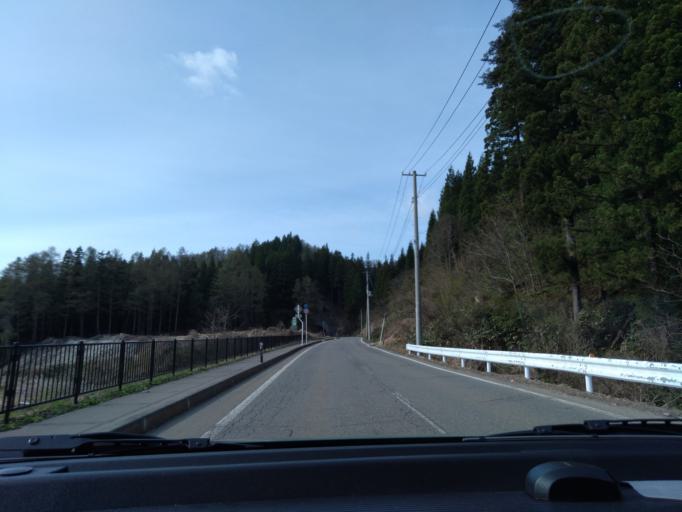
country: JP
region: Akita
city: Yokotemachi
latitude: 39.3096
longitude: 140.5848
